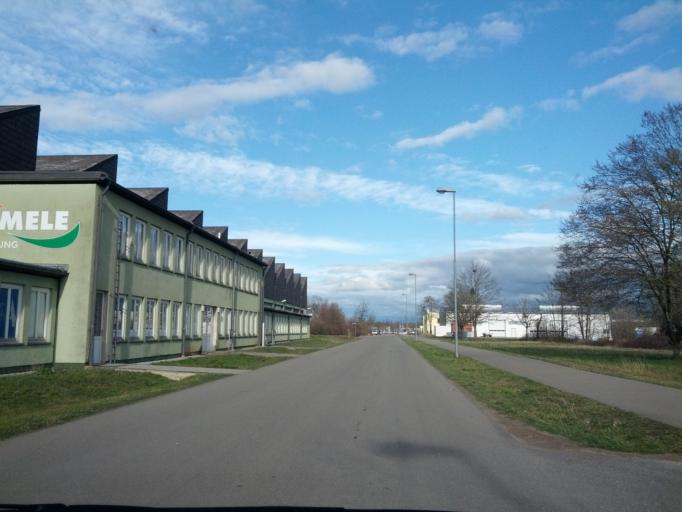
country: DE
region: Baden-Wuerttemberg
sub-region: Freiburg Region
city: Eschbach
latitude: 47.8962
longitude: 7.6182
